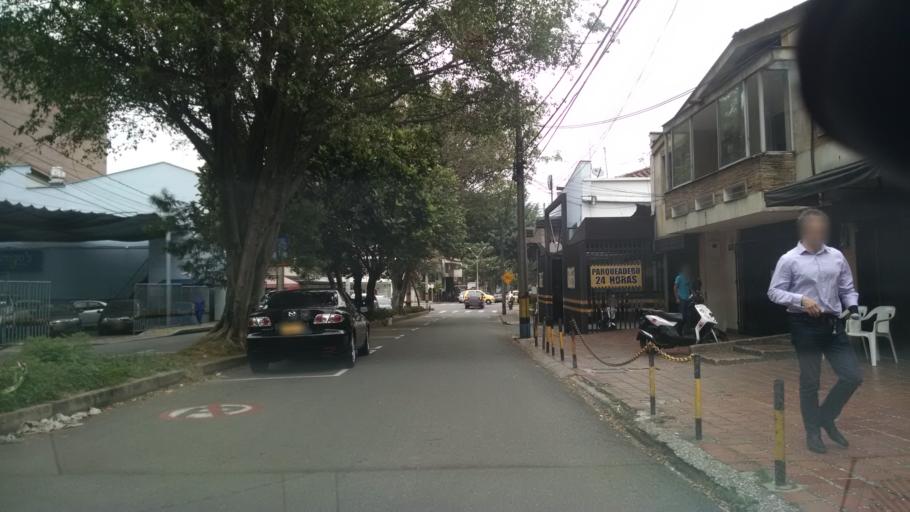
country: CO
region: Antioquia
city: Medellin
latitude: 6.2465
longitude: -75.5899
